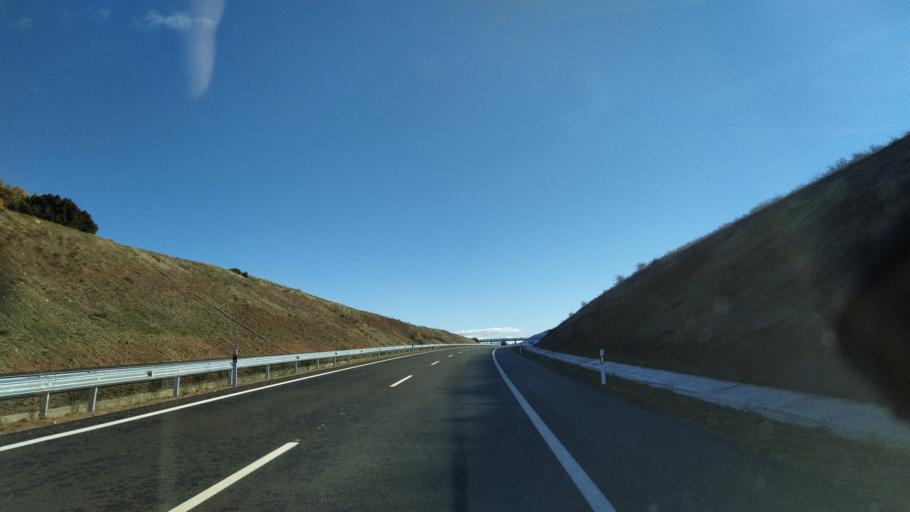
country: ES
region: Aragon
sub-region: Provincia de Huesca
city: Santa Cruz de la Seros
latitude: 42.5635
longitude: -0.6811
